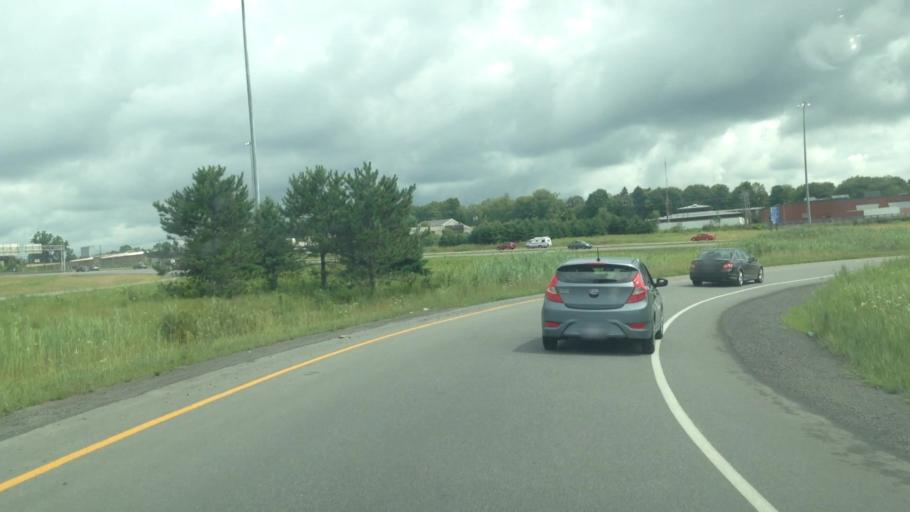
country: CA
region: Quebec
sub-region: Laurentides
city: Saint-Jerome
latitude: 45.7811
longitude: -74.0225
